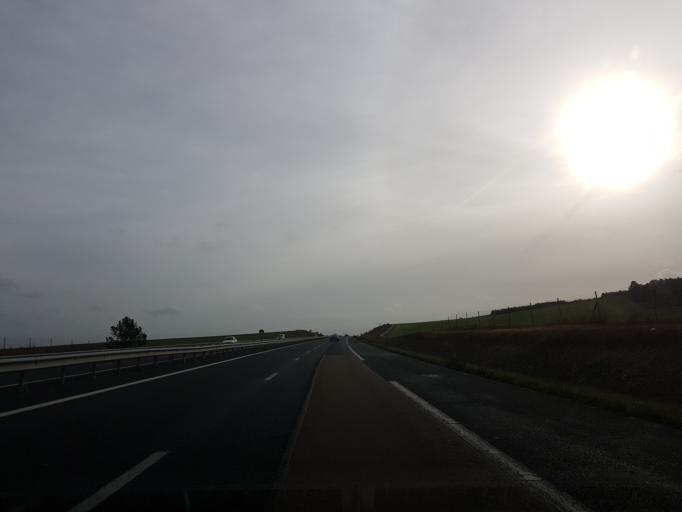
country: FR
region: Champagne-Ardenne
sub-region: Departement de l'Aube
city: La Riviere-de-Corps
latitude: 48.2651
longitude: 3.9673
